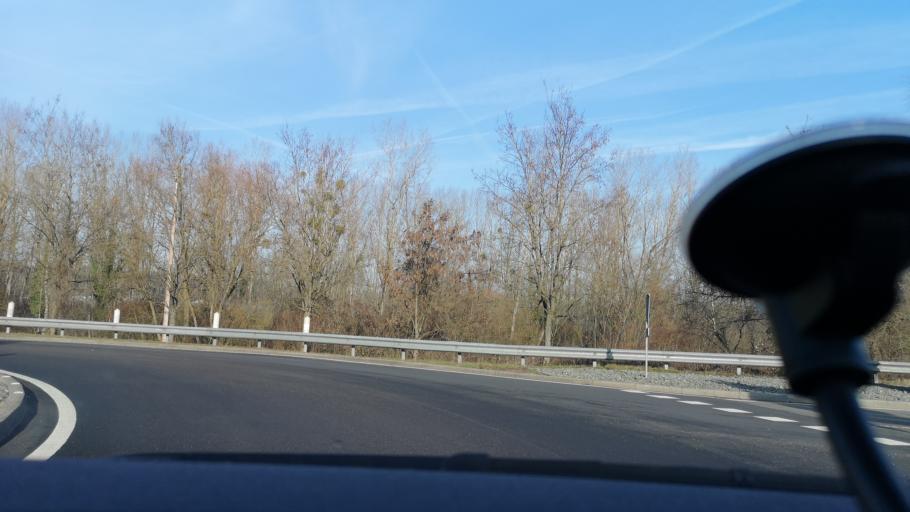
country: FR
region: Franche-Comte
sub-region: Departement du Doubs
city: Arbouans
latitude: 47.4847
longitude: 6.7988
